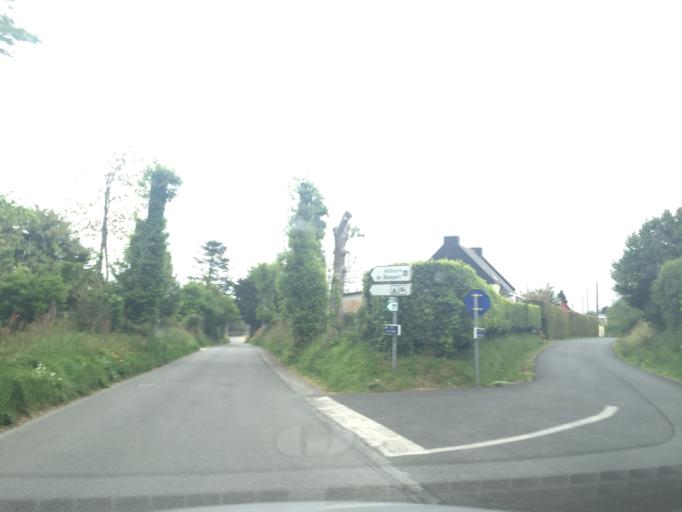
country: FR
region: Brittany
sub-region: Departement des Cotes-d'Armor
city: Paimpol
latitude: 48.7724
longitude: -3.0264
